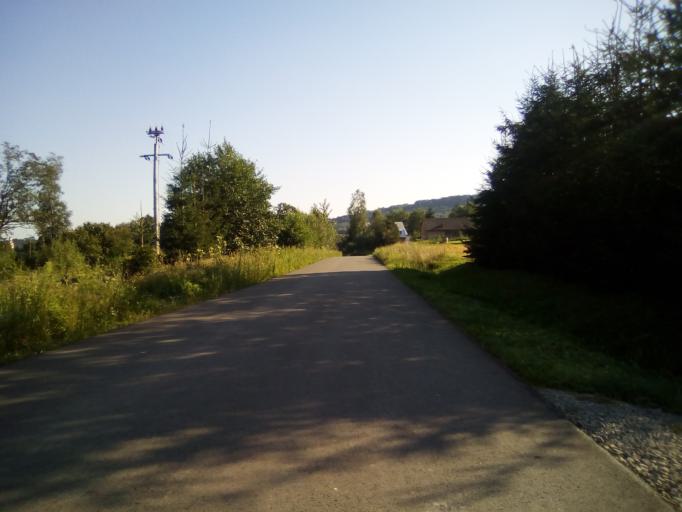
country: PL
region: Subcarpathian Voivodeship
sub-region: Powiat brzozowski
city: Domaradz
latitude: 49.8013
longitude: 21.9392
